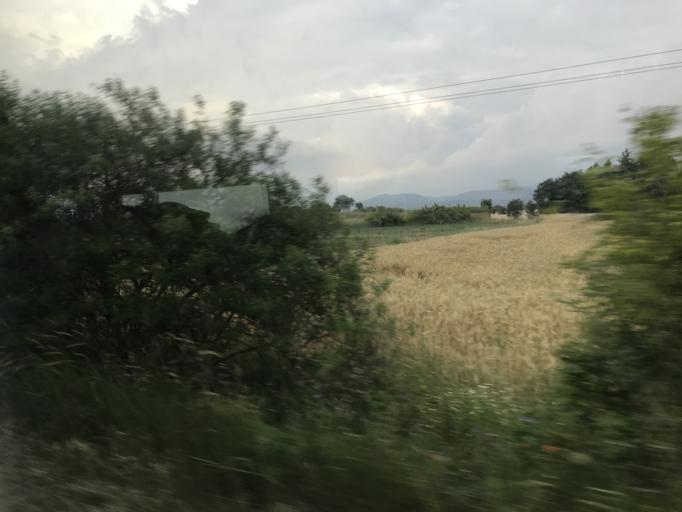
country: GR
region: East Macedonia and Thrace
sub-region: Nomos Rodopis
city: Sapes
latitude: 40.9755
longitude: 25.6455
